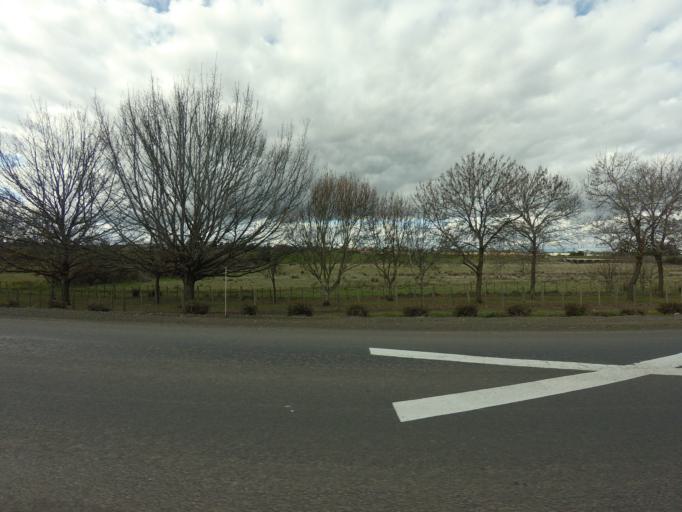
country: AU
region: Tasmania
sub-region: Northern Midlands
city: Longford
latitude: -41.5864
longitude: 147.1178
